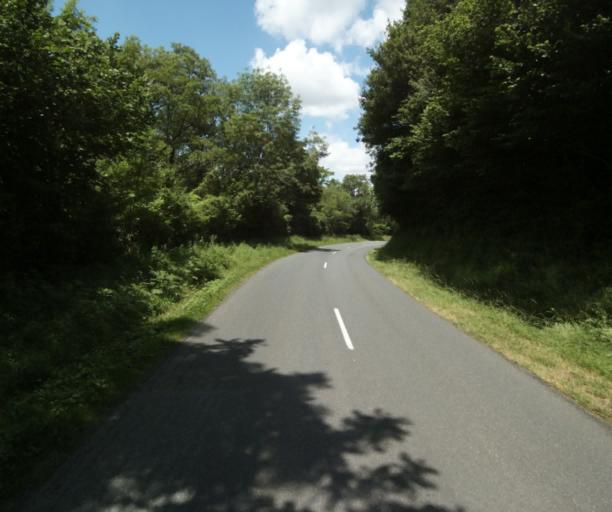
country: FR
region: Midi-Pyrenees
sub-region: Departement du Tarn
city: Soreze
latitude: 43.4277
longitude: 2.0570
